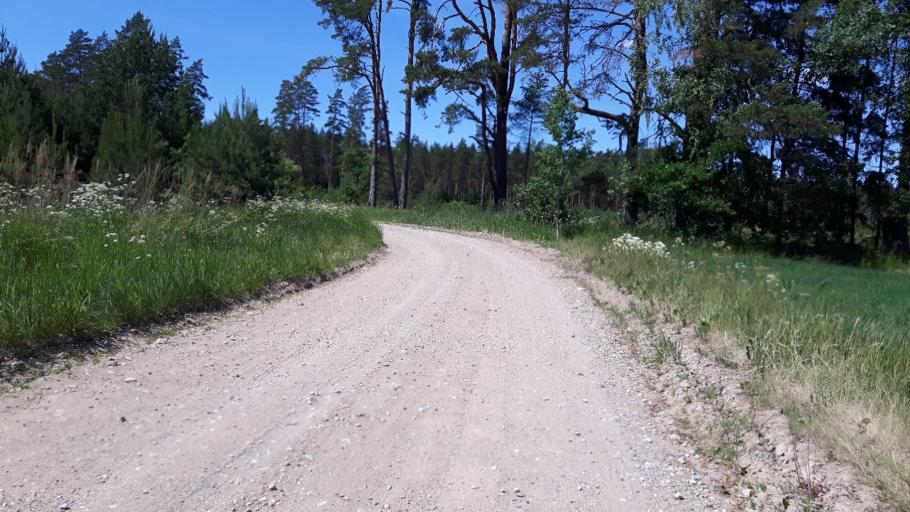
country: LV
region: Kandava
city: Kandava
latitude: 57.0413
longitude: 22.8168
